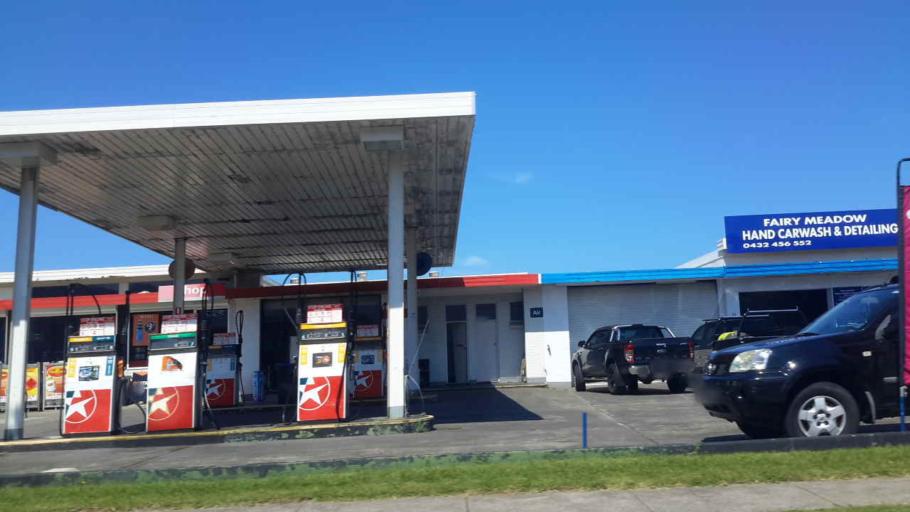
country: AU
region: New South Wales
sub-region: Wollongong
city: Fairy Meadow
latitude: -34.3892
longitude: 150.8939
